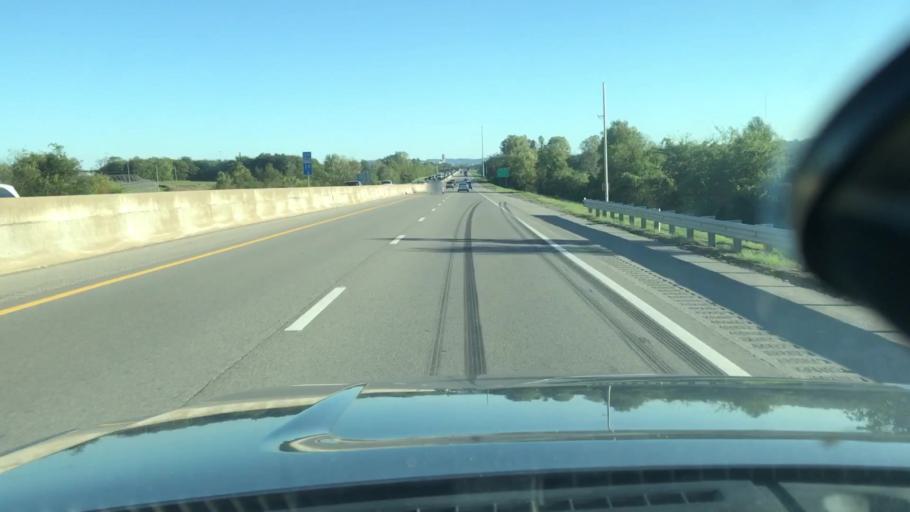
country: US
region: Tennessee
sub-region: Davidson County
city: Nashville
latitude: 36.2014
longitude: -86.8690
